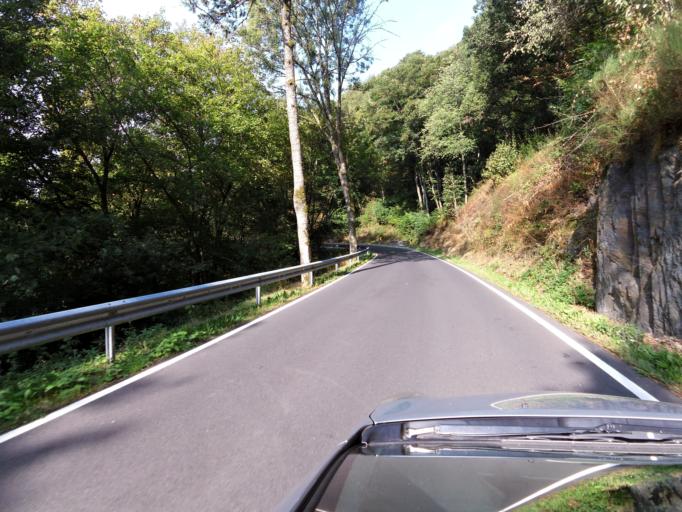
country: LU
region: Diekirch
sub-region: Canton de Wiltz
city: Goesdorf
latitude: 49.9125
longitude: 5.9784
